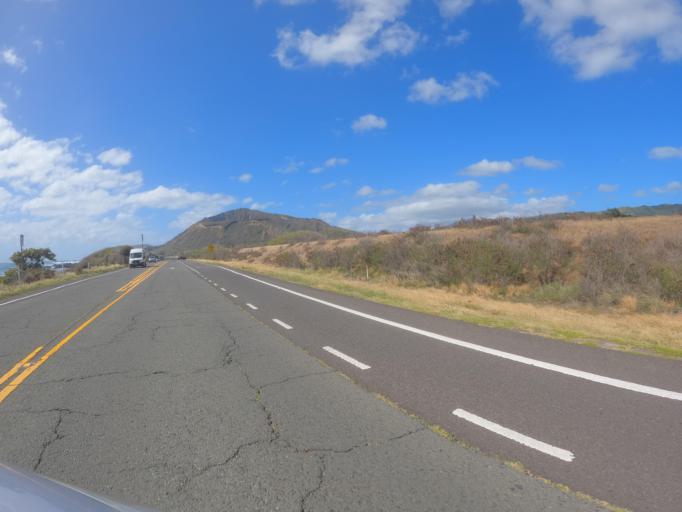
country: US
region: Hawaii
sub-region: Honolulu County
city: Waimanalo Beach
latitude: 21.2914
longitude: -157.6639
